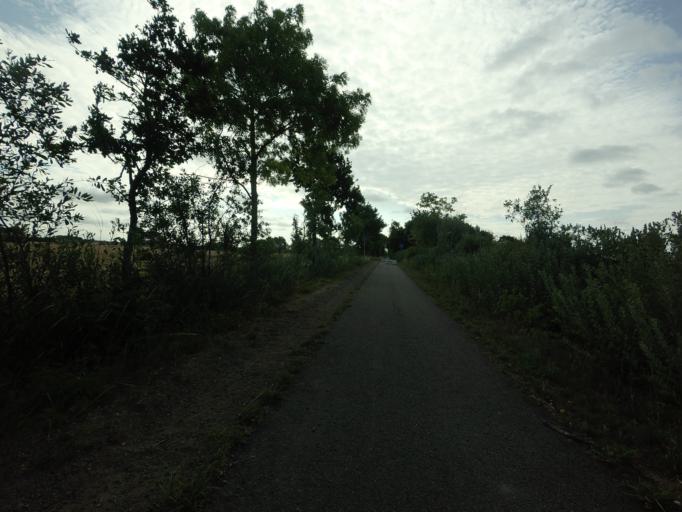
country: SE
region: Skane
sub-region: Helsingborg
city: Odakra
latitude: 56.1796
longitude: 12.6662
